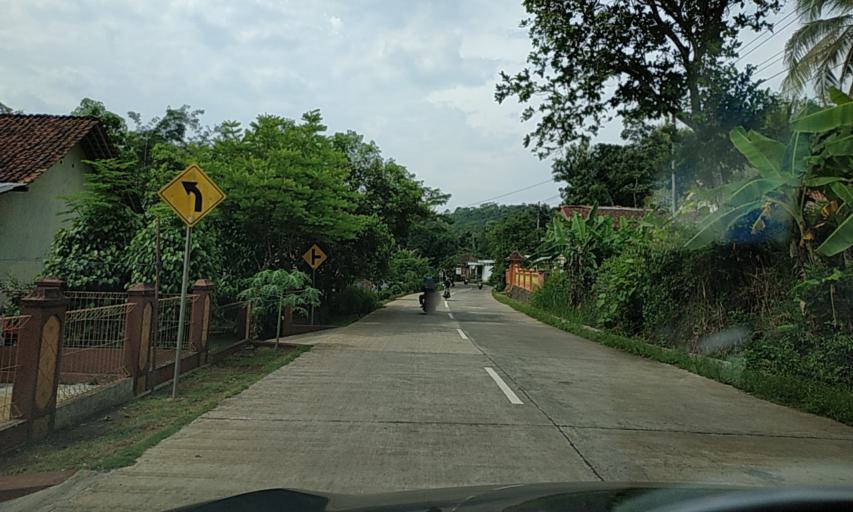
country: ID
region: Central Java
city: Winangun
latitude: -7.3651
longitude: 108.7006
